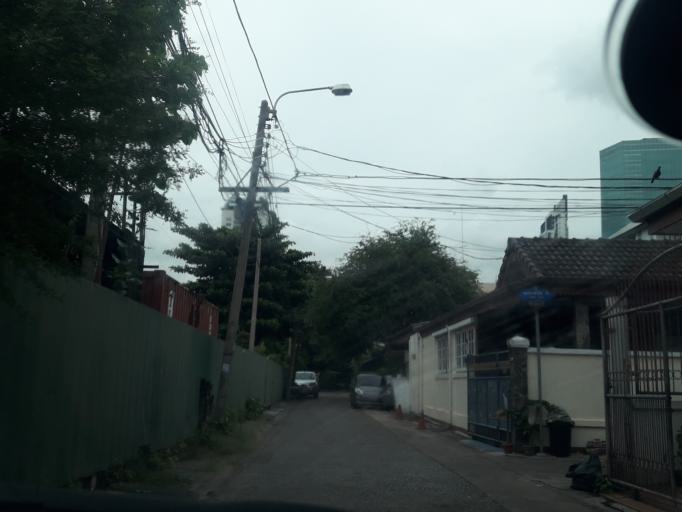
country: TH
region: Bangkok
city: Chatuchak
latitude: 13.8288
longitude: 100.5608
